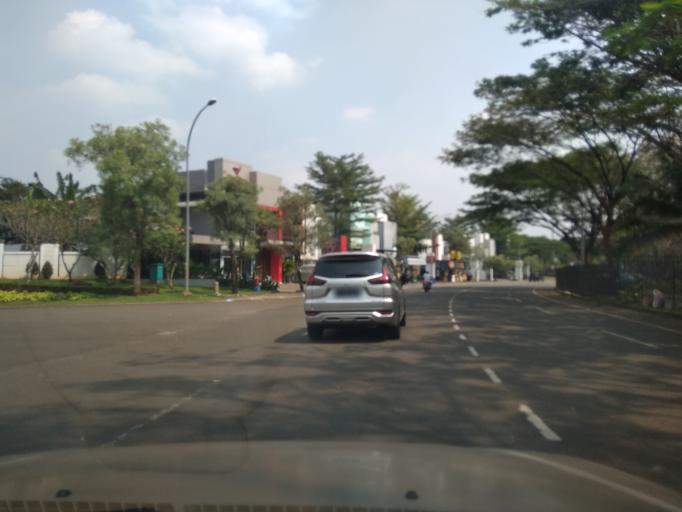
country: ID
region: West Java
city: Serpong
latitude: -6.3151
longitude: 106.6468
